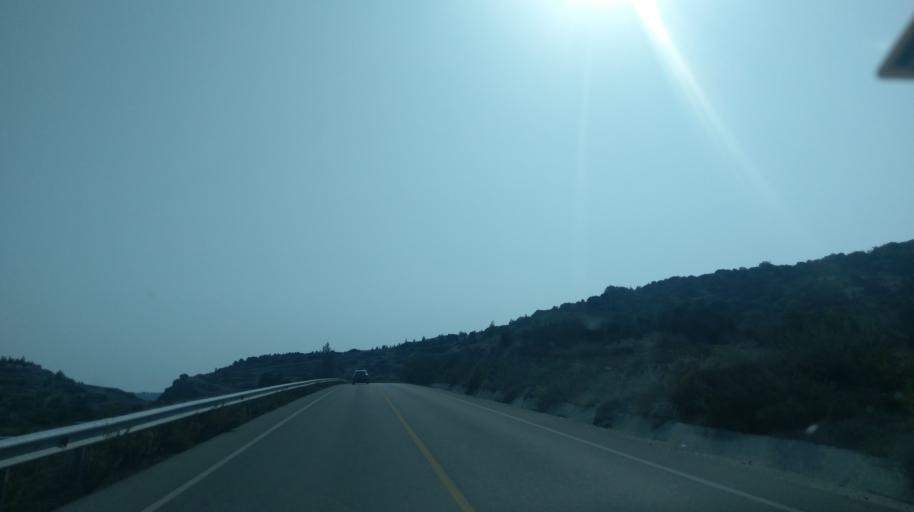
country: CY
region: Ammochostos
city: Leonarisso
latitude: 35.4841
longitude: 34.1034
